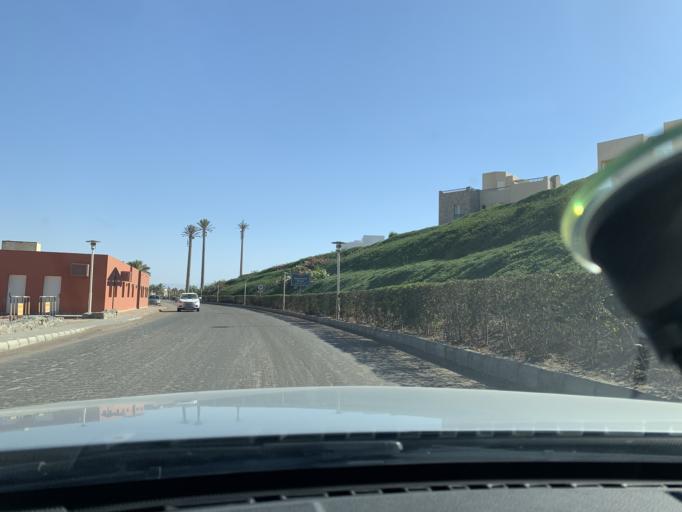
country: EG
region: Red Sea
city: El Gouna
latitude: 27.4084
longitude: 33.6729
